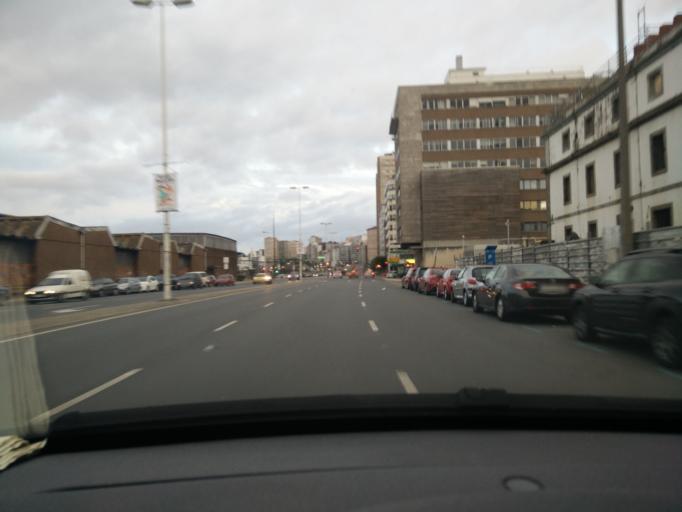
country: ES
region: Galicia
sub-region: Provincia da Coruna
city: A Coruna
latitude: 43.3585
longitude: -8.4012
